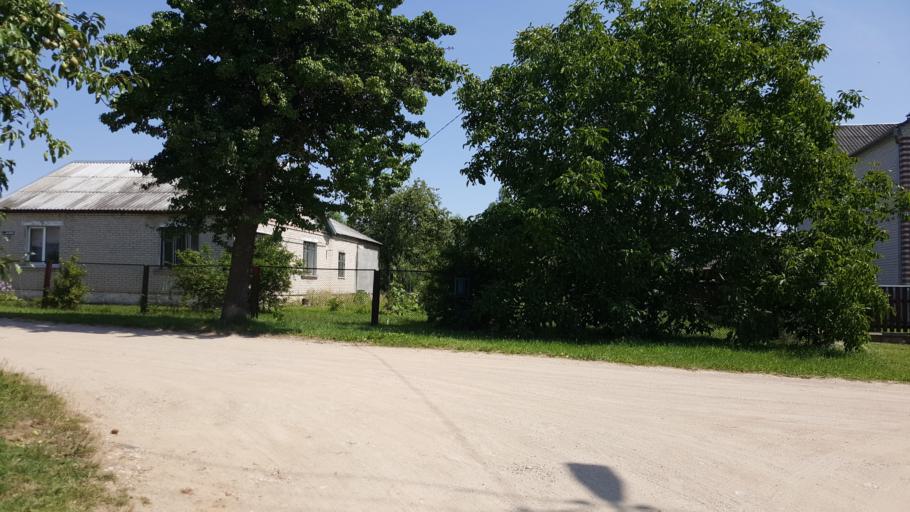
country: BY
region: Brest
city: Vysokaye
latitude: 52.3614
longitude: 23.3879
